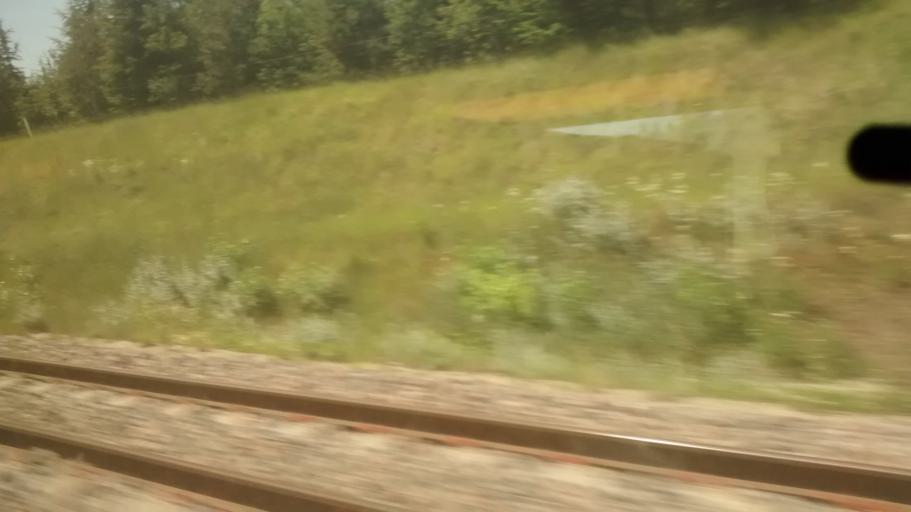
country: FR
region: Rhone-Alpes
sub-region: Departement de la Drome
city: Montboucher-sur-Jabron
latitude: 44.5392
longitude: 4.8152
